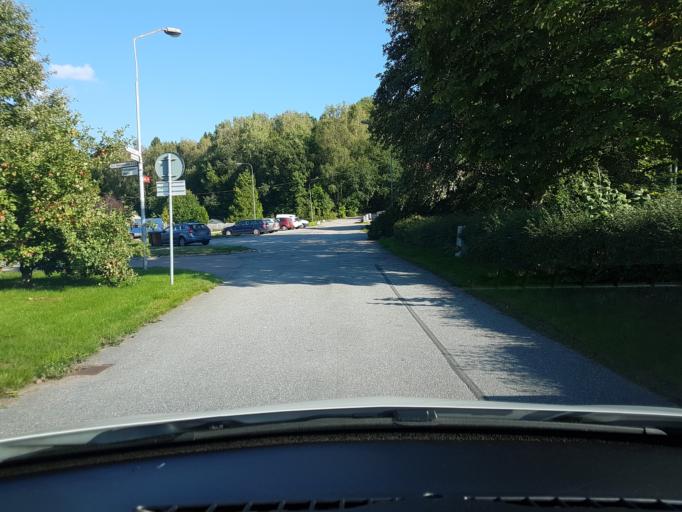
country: SE
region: Vaestra Goetaland
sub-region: Ale Kommun
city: Skepplanda
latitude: 57.9790
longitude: 12.2017
